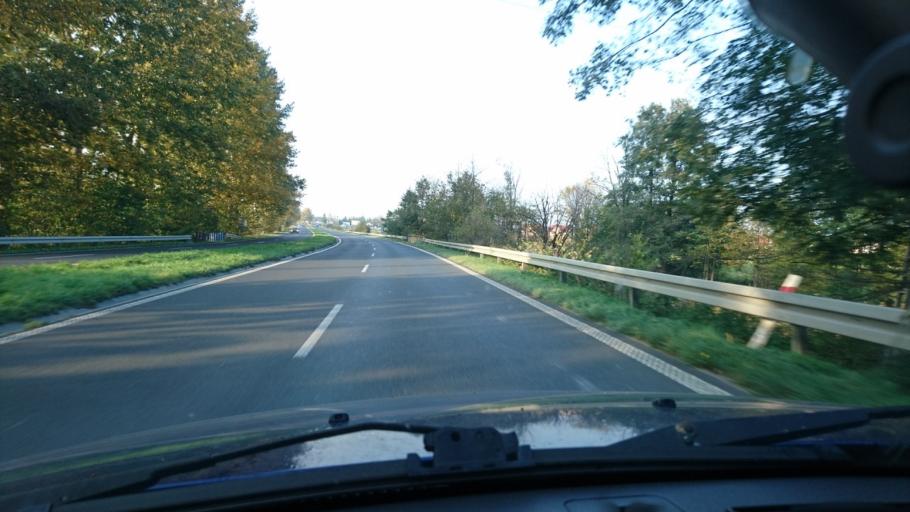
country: PL
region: Silesian Voivodeship
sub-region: Powiat cieszynski
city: Ustron
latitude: 49.7300
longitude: 18.7940
